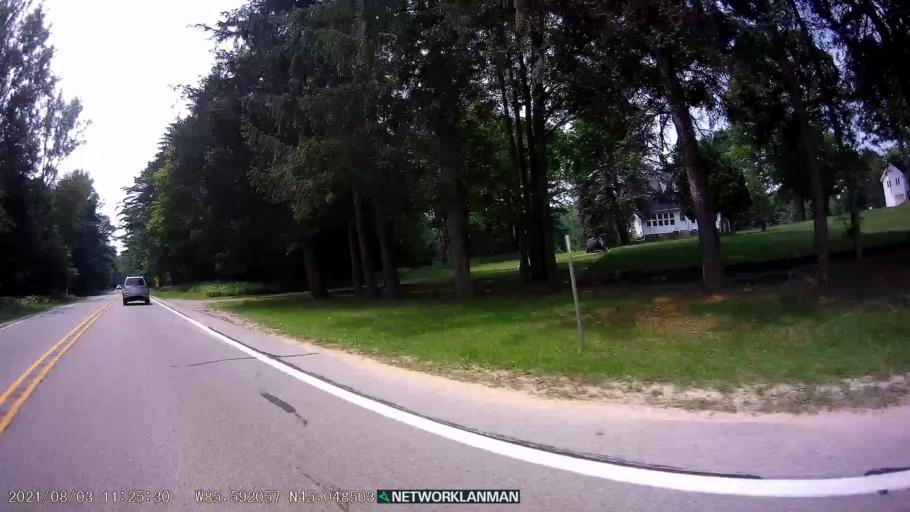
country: US
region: Michigan
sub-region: Leelanau County
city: Leland
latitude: 45.0483
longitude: -85.5924
